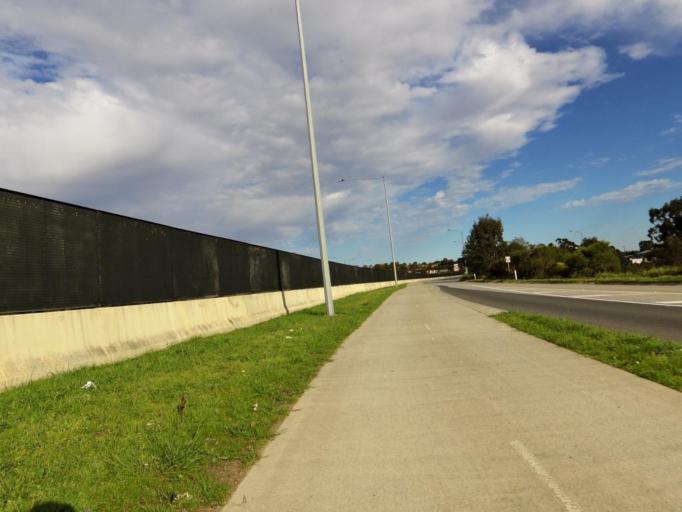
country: AU
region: Victoria
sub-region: Knox
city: Wantirna South
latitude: -37.8806
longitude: 145.2135
